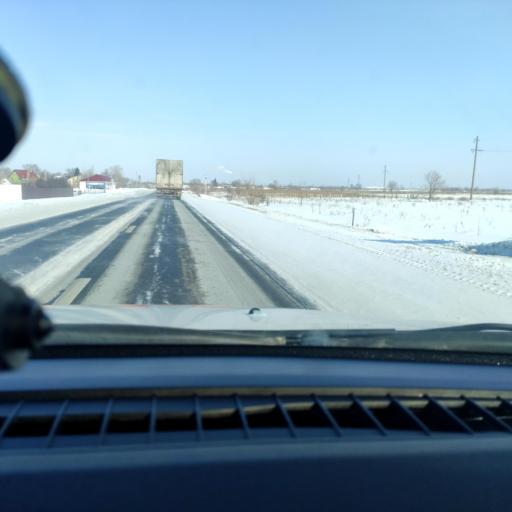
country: RU
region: Samara
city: Smyshlyayevka
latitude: 53.1767
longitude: 50.4604
